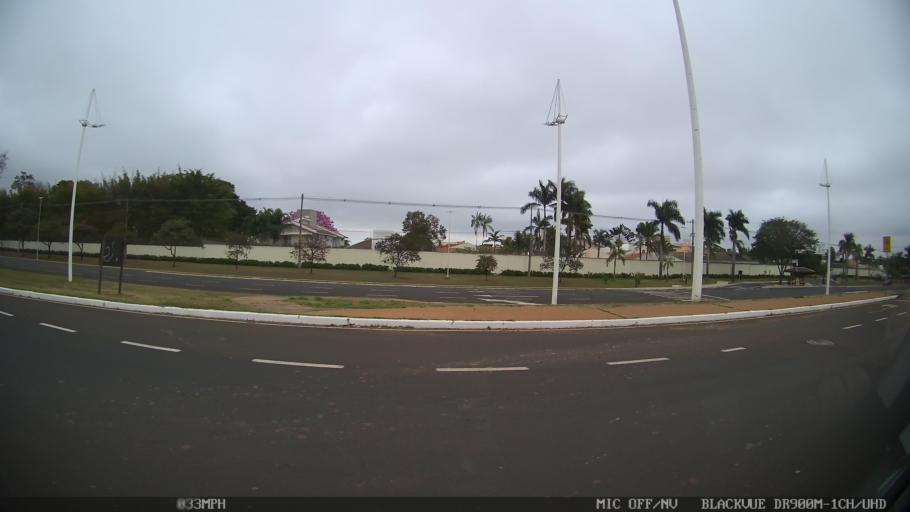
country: BR
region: Sao Paulo
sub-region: Sao Jose Do Rio Preto
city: Sao Jose do Rio Preto
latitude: -20.8471
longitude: -49.4032
